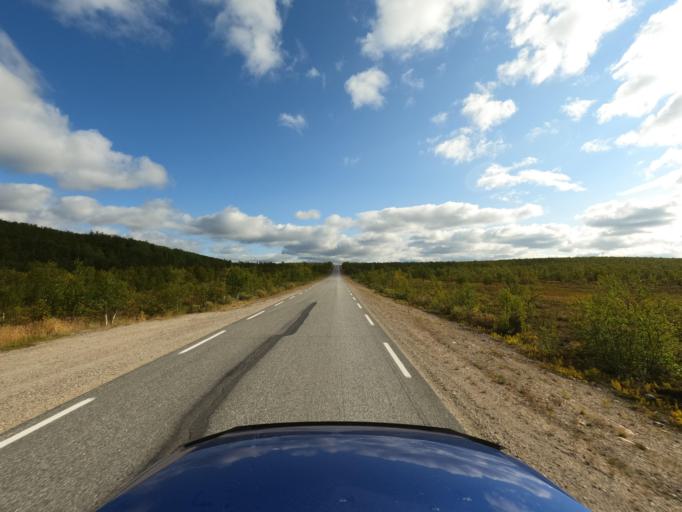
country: NO
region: Finnmark Fylke
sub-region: Porsanger
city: Lakselv
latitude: 69.3908
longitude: 24.5092
